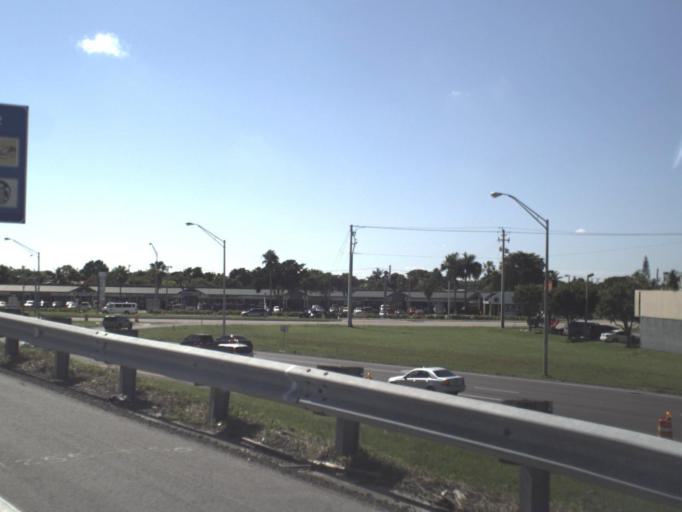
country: US
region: Florida
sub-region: Miami-Dade County
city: South Miami Heights
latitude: 25.5992
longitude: -80.3764
